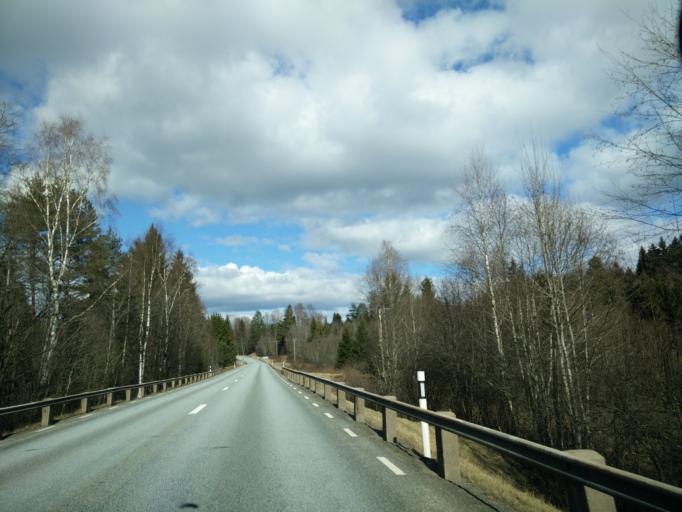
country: SE
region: Vaermland
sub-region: Munkfors Kommun
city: Munkfors
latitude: 59.9114
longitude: 13.5688
